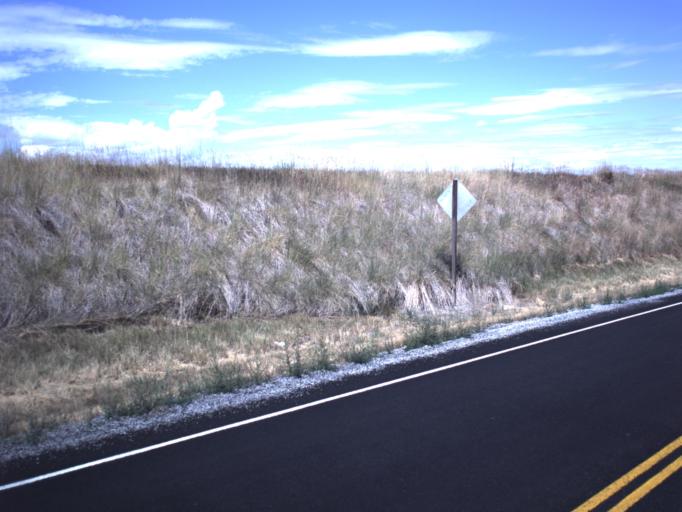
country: US
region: Utah
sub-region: Box Elder County
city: Garland
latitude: 41.8302
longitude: -112.1457
